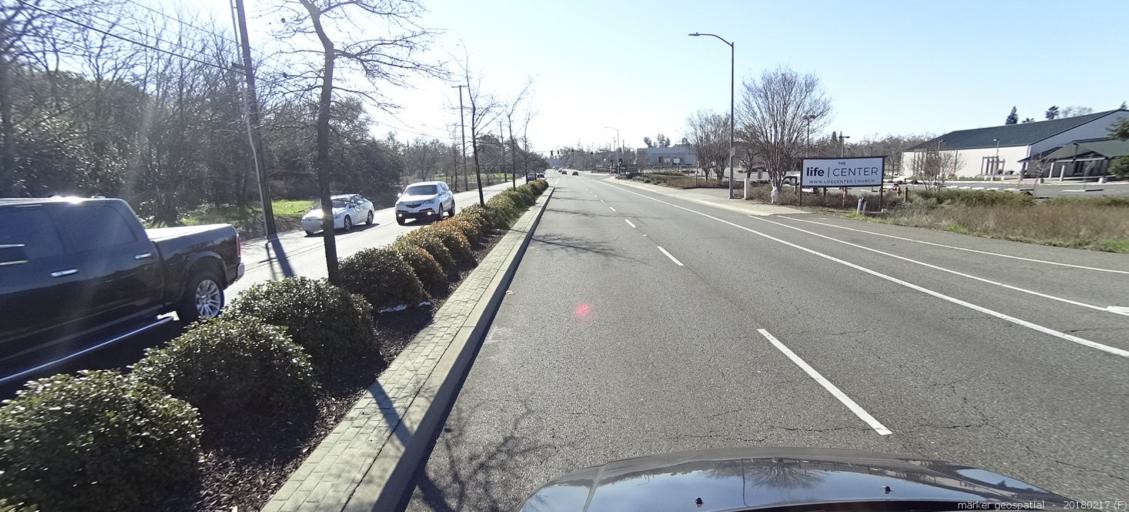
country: US
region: California
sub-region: Sacramento County
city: Orangevale
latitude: 38.7090
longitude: -121.2256
